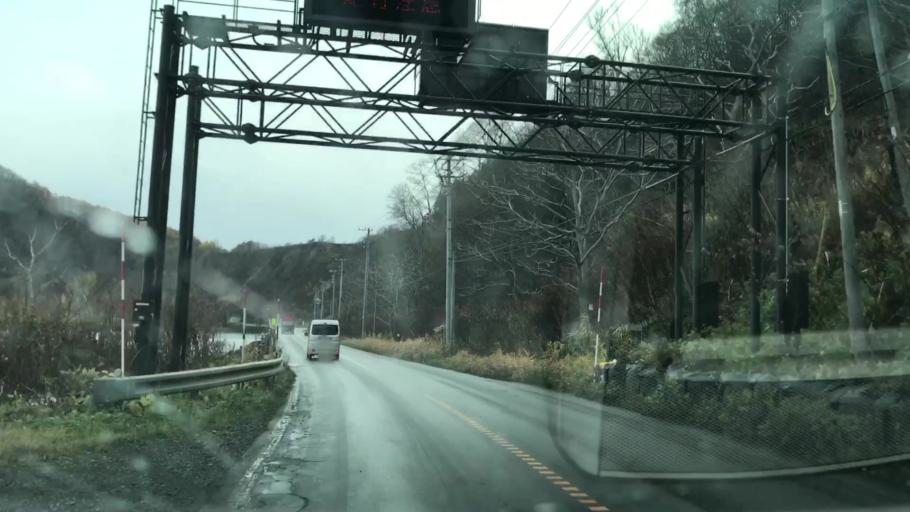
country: JP
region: Hokkaido
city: Yoichi
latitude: 43.2903
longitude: 140.6323
